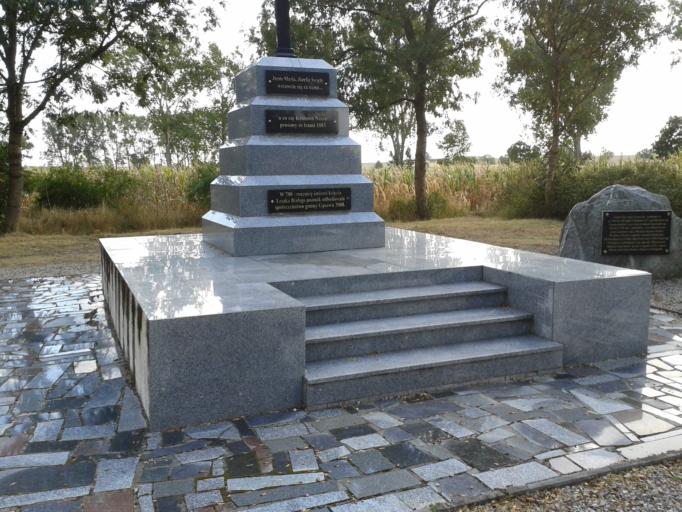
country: PL
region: Kujawsko-Pomorskie
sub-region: Powiat zninski
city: Gasawa
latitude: 52.7688
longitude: 17.7334
